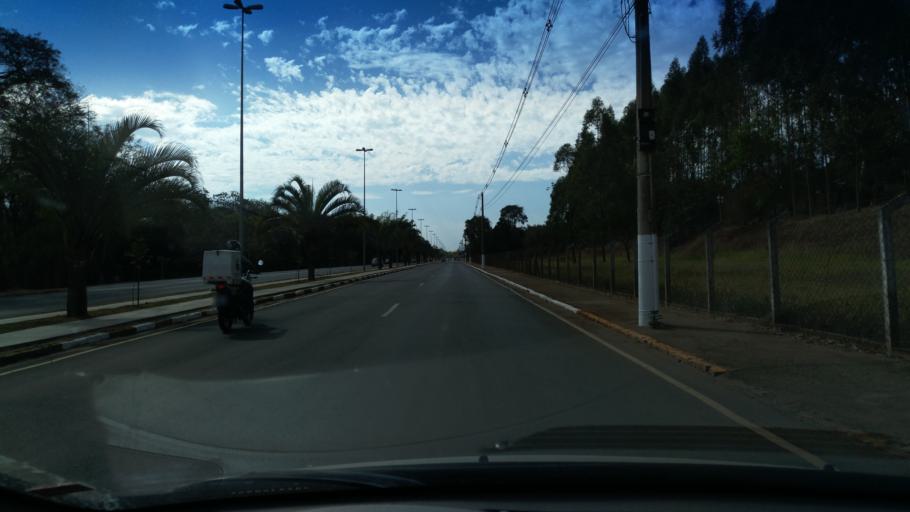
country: BR
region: Sao Paulo
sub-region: Jaguariuna
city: Jaguariuna
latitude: -22.6305
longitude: -47.0614
